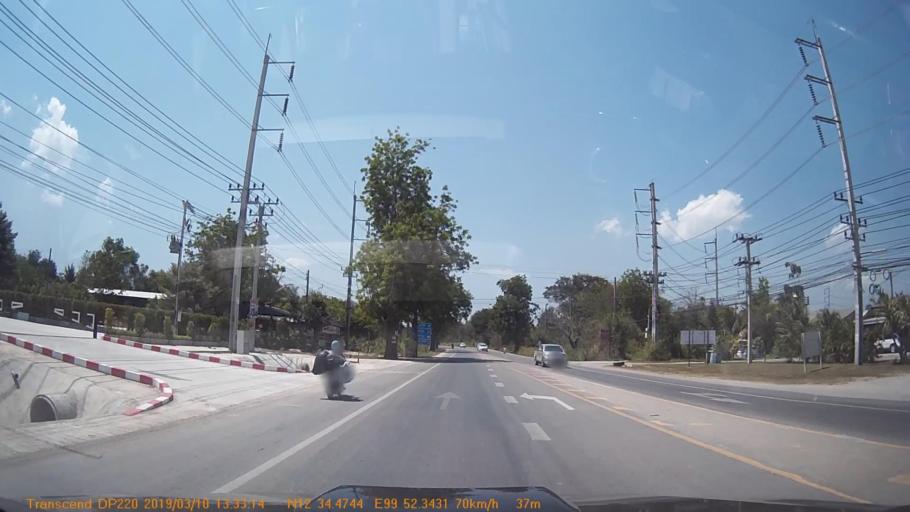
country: TH
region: Prachuap Khiri Khan
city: Hua Hin
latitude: 12.5747
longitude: 99.8721
